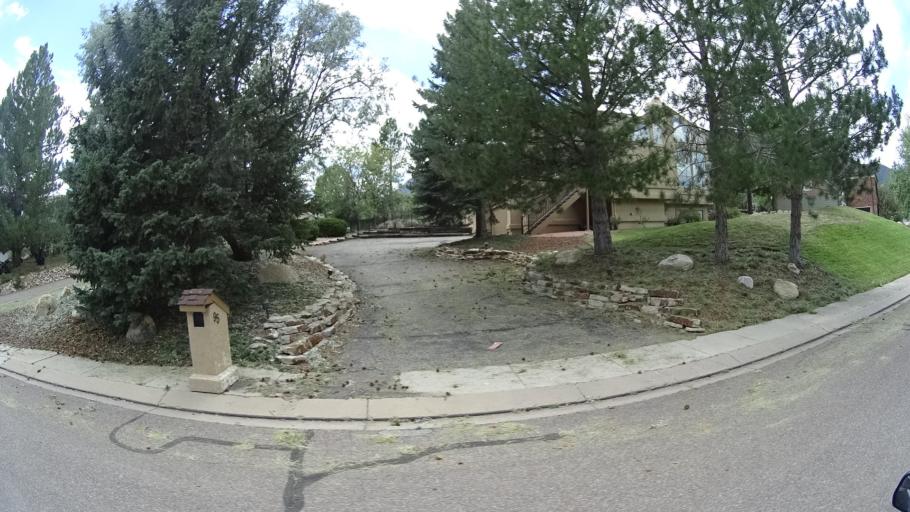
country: US
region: Colorado
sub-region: El Paso County
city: Stratmoor
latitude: 38.7743
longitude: -104.8281
